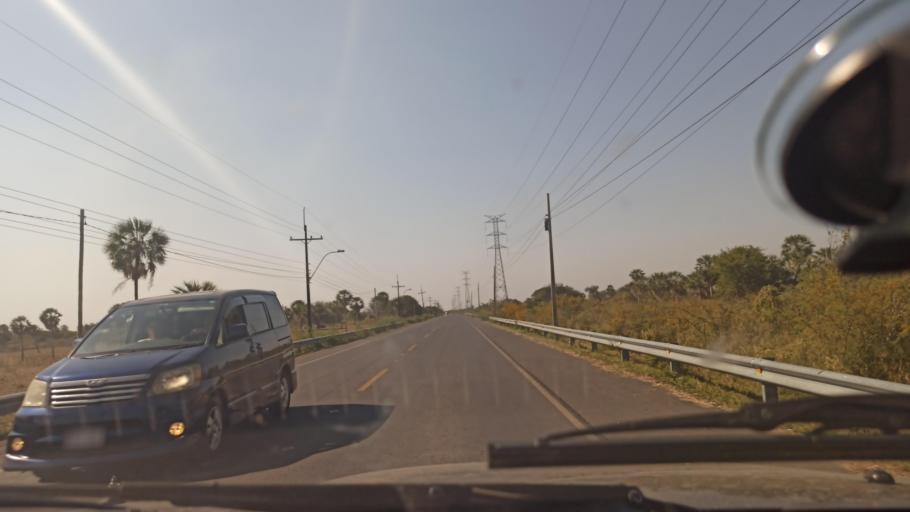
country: PY
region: Presidente Hayes
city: Nanawa
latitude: -25.2563
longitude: -57.6774
